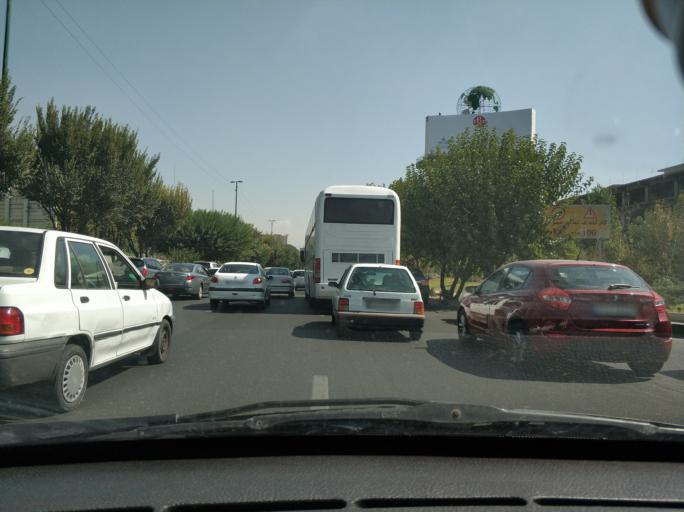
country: IR
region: Tehran
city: Tehran
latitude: 35.7498
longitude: 51.3811
